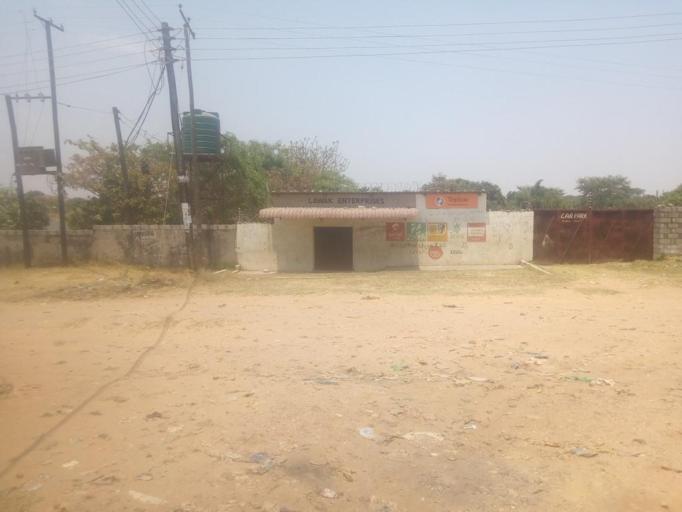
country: ZM
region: Lusaka
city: Lusaka
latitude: -15.4093
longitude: 28.3747
